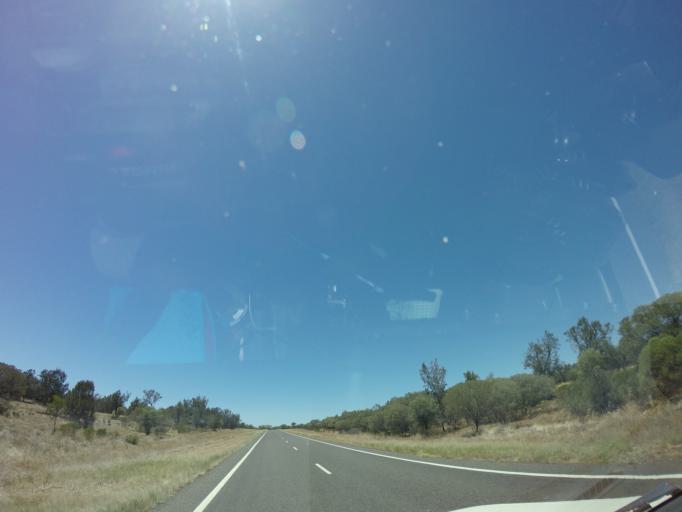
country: AU
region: New South Wales
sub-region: Cobar
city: Cobar
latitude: -31.5731
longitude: 144.7970
